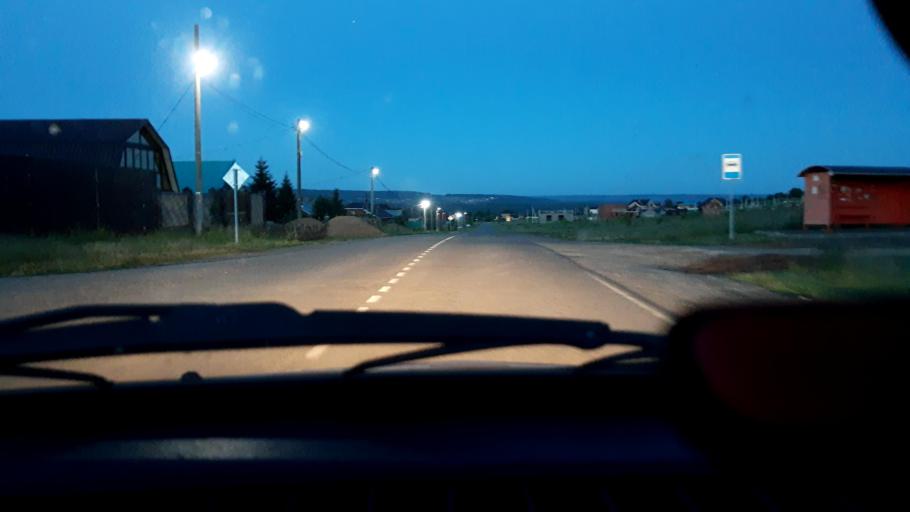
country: RU
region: Bashkortostan
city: Avdon
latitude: 54.6330
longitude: 55.6964
